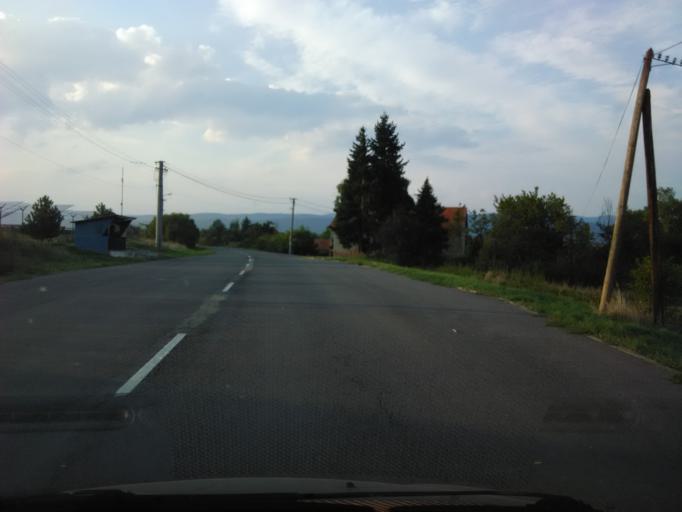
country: SK
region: Nitriansky
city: Levice
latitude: 48.2822
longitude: 18.6911
